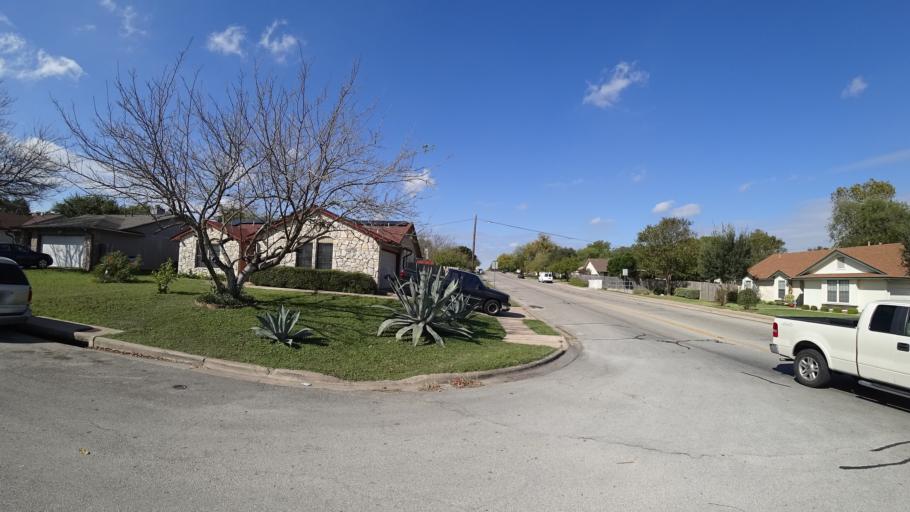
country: US
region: Texas
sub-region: Travis County
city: Windemere
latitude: 30.4536
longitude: -97.6474
